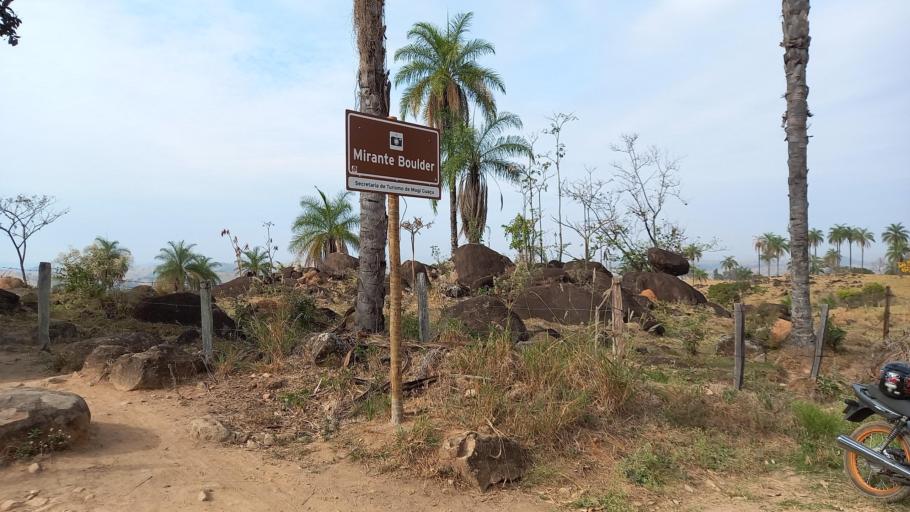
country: BR
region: Sao Paulo
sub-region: Itapira
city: Itapira
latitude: -22.2912
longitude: -46.8169
